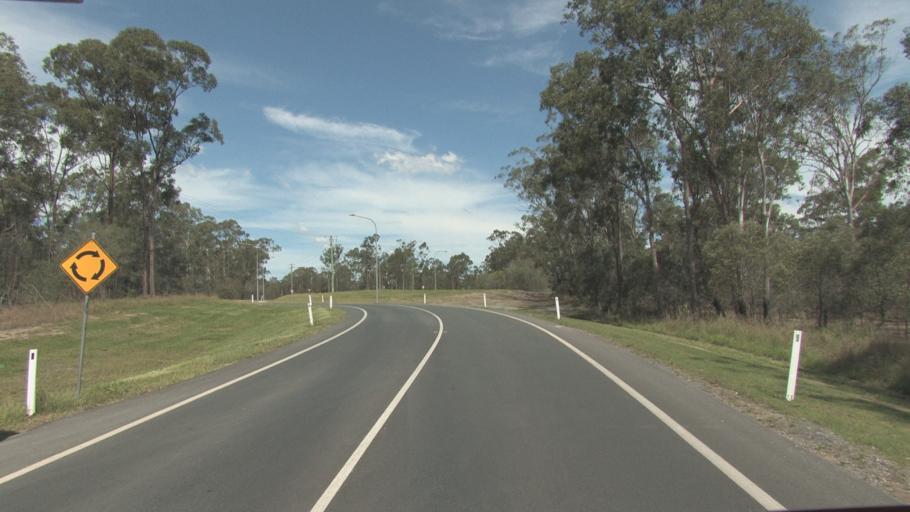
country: AU
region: Queensland
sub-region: Logan
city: Cedar Vale
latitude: -27.8349
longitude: 153.0446
